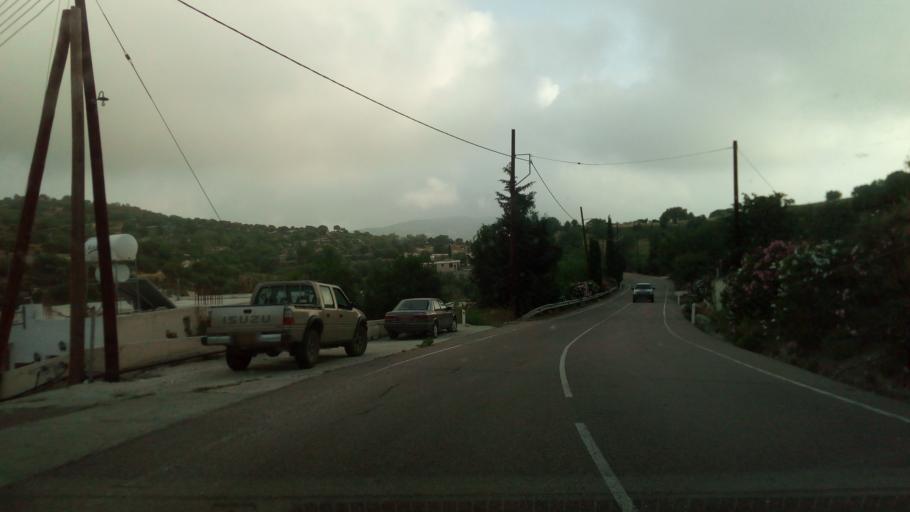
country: CY
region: Limassol
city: Pachna
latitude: 34.8353
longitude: 32.6869
